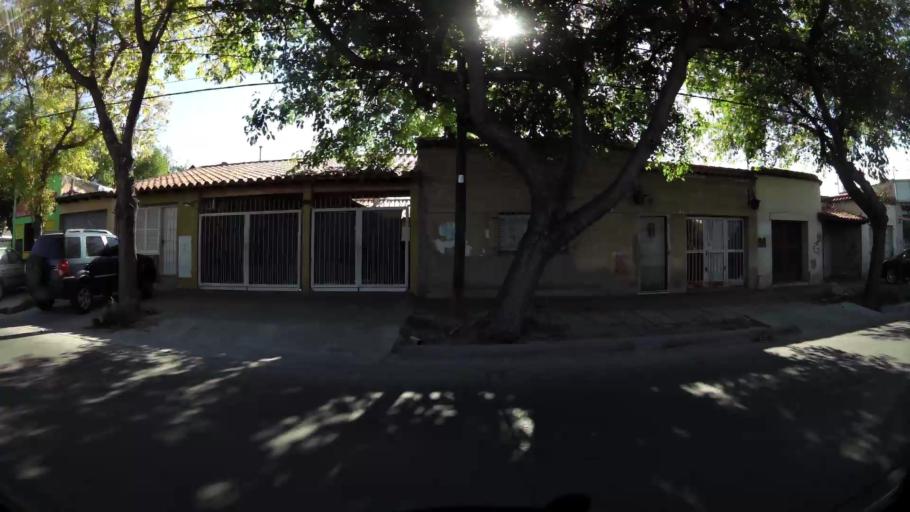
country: AR
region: Mendoza
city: Mendoza
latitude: -32.9006
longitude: -68.8244
